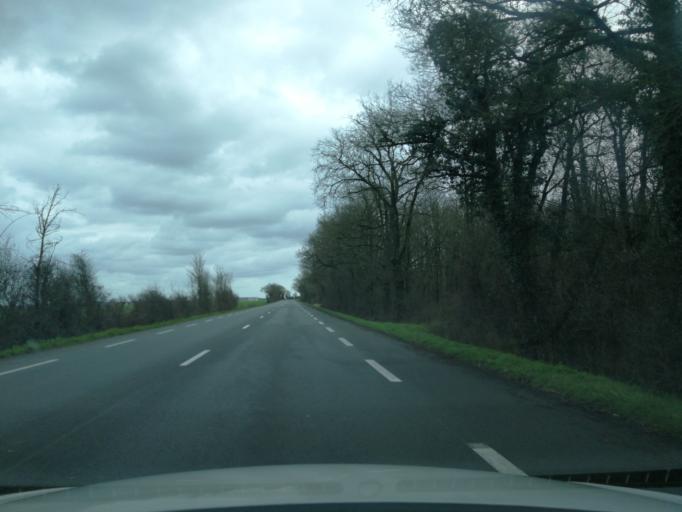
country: FR
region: Pays de la Loire
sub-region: Departement de la Vendee
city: Chavagnes-en-Paillers
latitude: 46.9234
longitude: -1.2524
